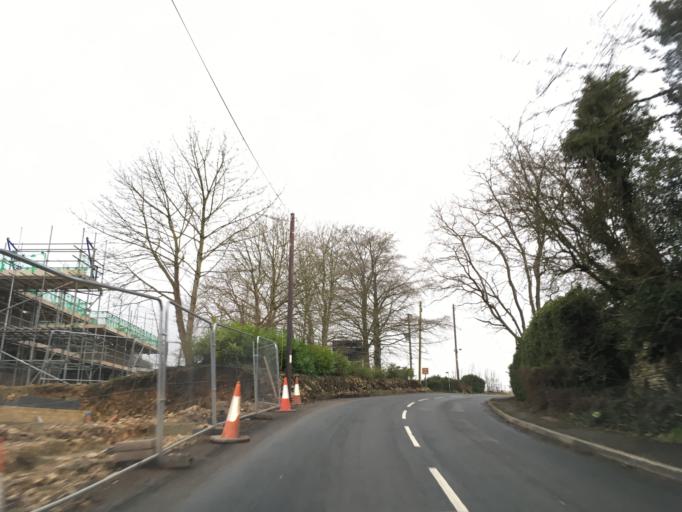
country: GB
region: England
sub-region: Gloucestershire
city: Nailsworth
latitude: 51.6824
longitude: -2.2441
